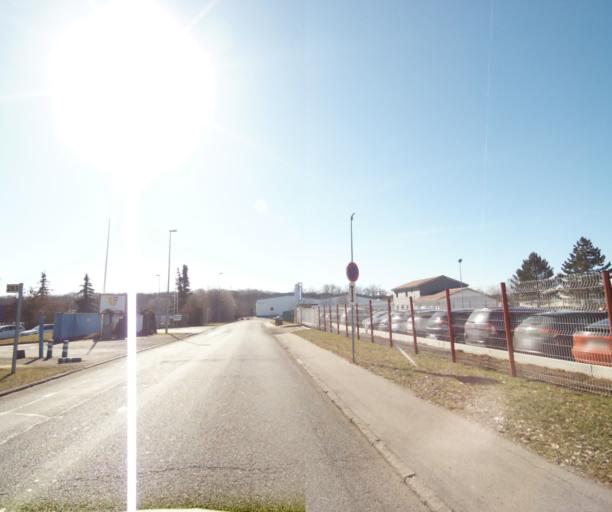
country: FR
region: Lorraine
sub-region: Departement de Meurthe-et-Moselle
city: Richardmenil
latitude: 48.6106
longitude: 6.1857
